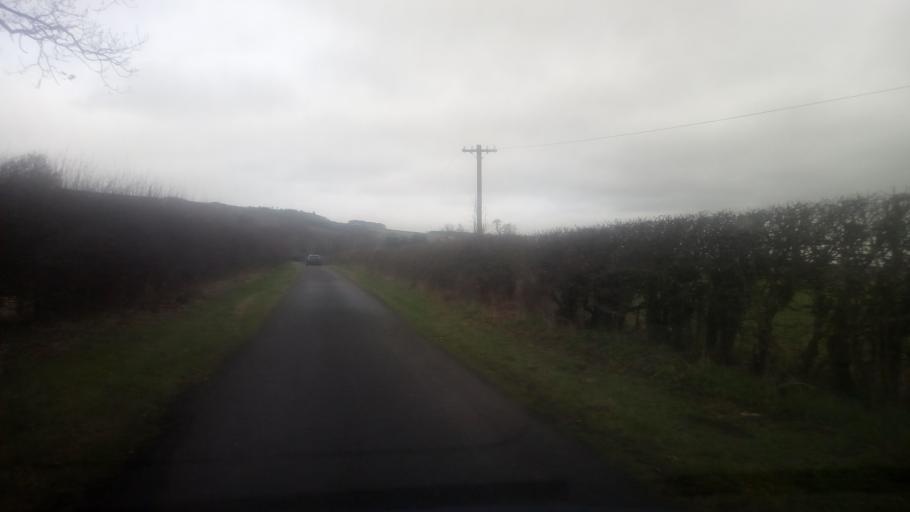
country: GB
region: Scotland
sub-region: The Scottish Borders
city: Jedburgh
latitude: 55.5051
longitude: -2.5373
